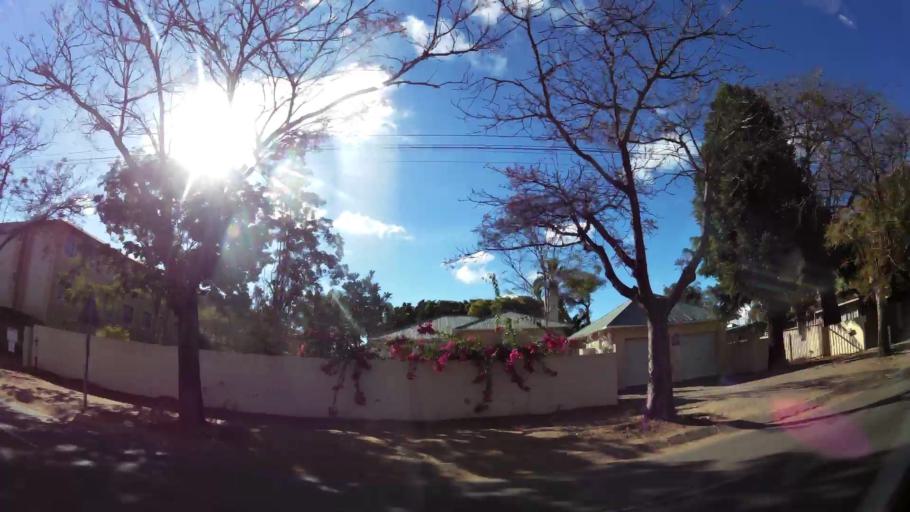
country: ZA
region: Limpopo
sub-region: Capricorn District Municipality
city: Polokwane
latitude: -23.9024
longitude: 29.4583
